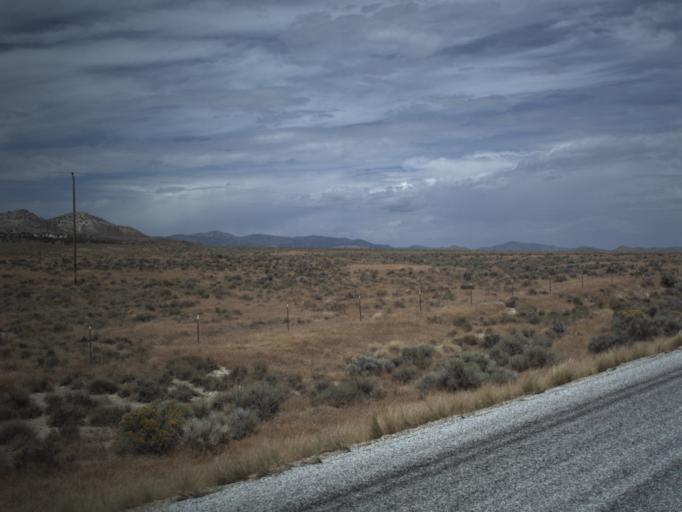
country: US
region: Utah
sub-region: Tooele County
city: Wendover
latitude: 41.5104
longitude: -113.6010
